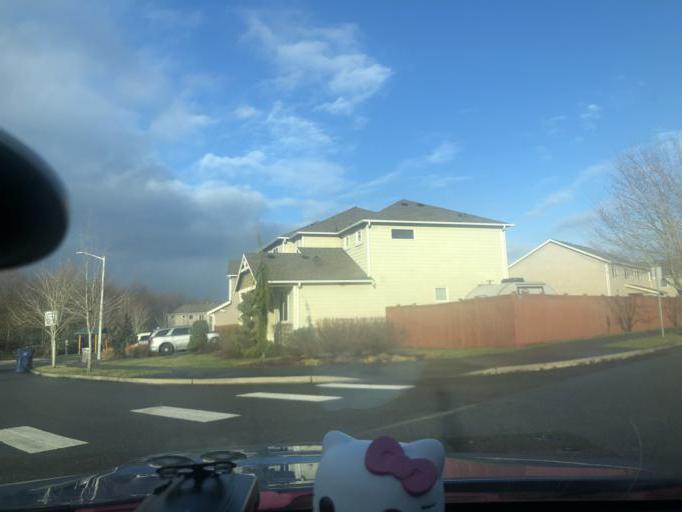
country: US
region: Washington
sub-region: Snohomish County
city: Sisco Heights
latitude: 48.1523
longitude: -122.1167
